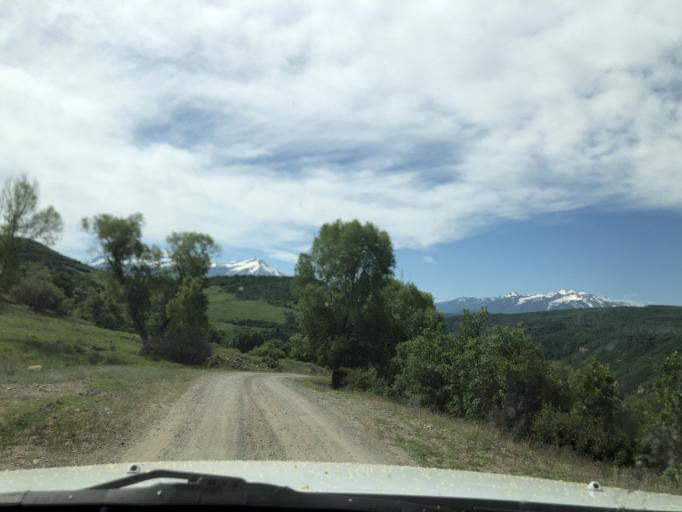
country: US
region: Colorado
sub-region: Delta County
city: Paonia
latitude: 38.9999
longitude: -107.3461
